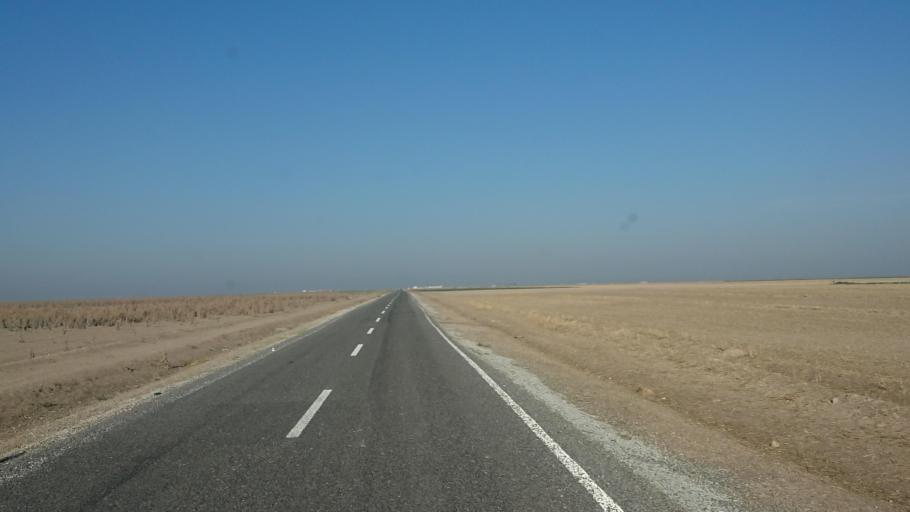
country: TR
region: Aksaray
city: Yesilova
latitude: 38.3879
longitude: 33.7723
